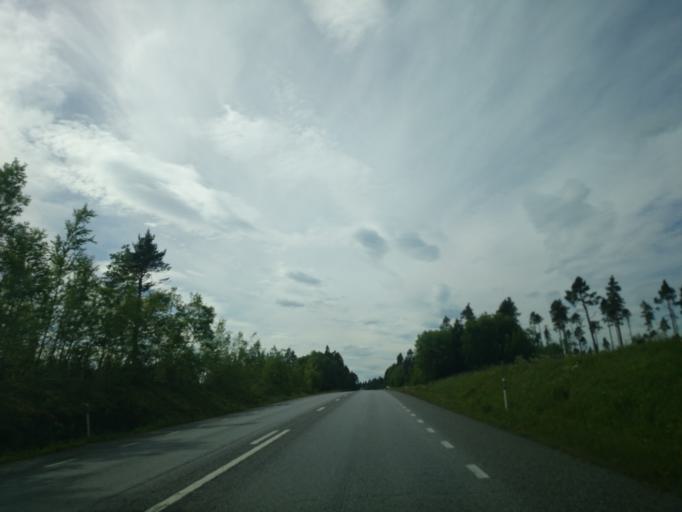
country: SE
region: Jaemtland
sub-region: Are Kommun
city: Jarpen
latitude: 63.3170
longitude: 13.5800
